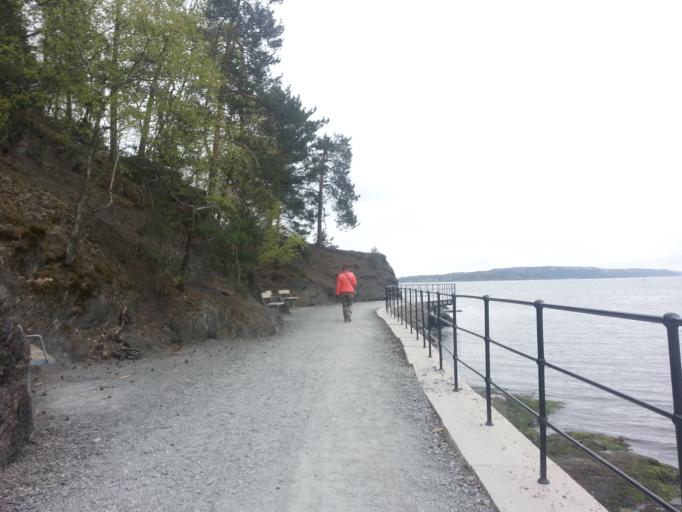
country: NO
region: Akershus
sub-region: Baerum
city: Lysaker
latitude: 59.9127
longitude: 10.6482
